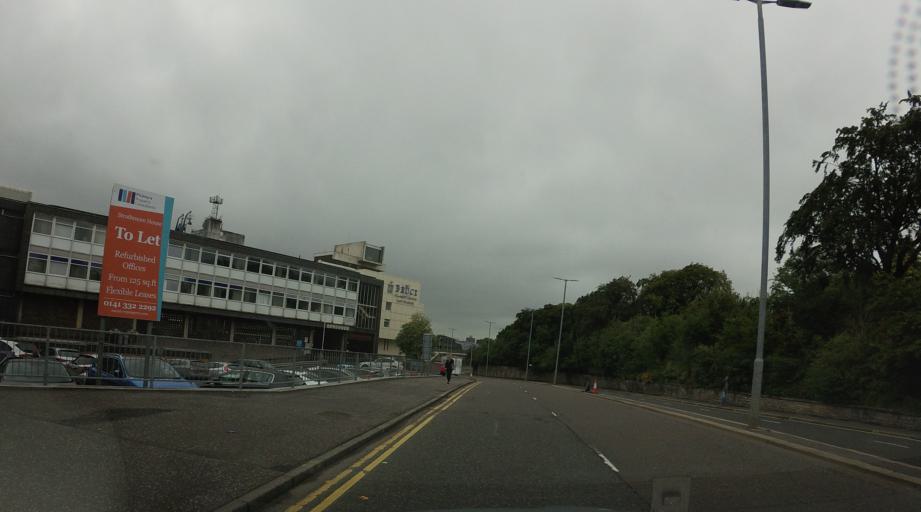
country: GB
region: Scotland
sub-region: South Lanarkshire
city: East Kilbride
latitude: 55.7616
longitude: -4.1778
